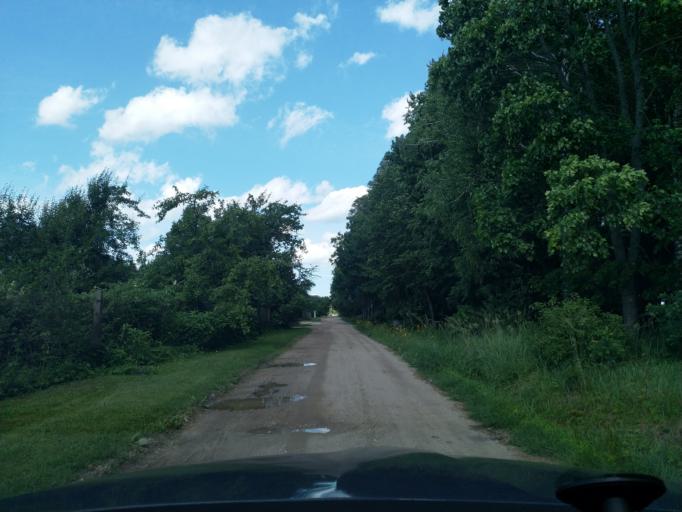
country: LV
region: Kuldigas Rajons
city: Kuldiga
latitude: 56.9520
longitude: 22.0021
